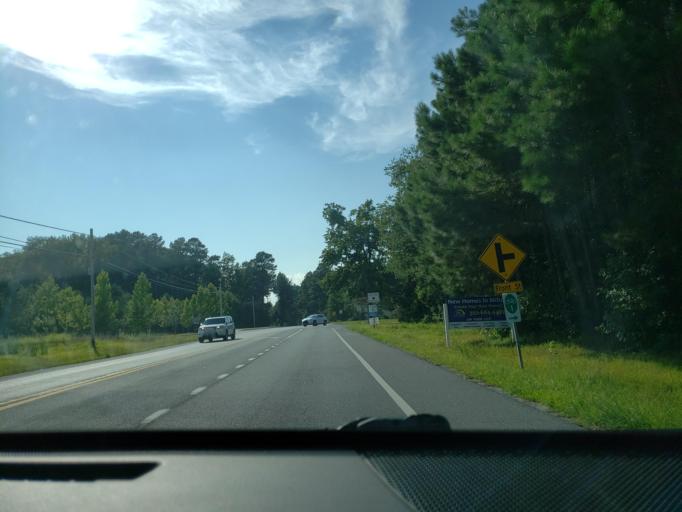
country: US
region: Delaware
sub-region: Sussex County
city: Milton
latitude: 38.7716
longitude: -75.2998
